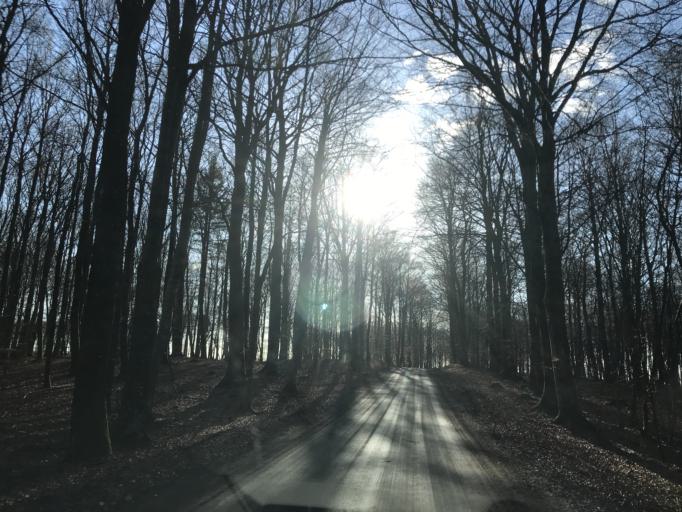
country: SE
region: Skane
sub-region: Ystads Kommun
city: Ystad
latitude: 55.5584
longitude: 13.8199
